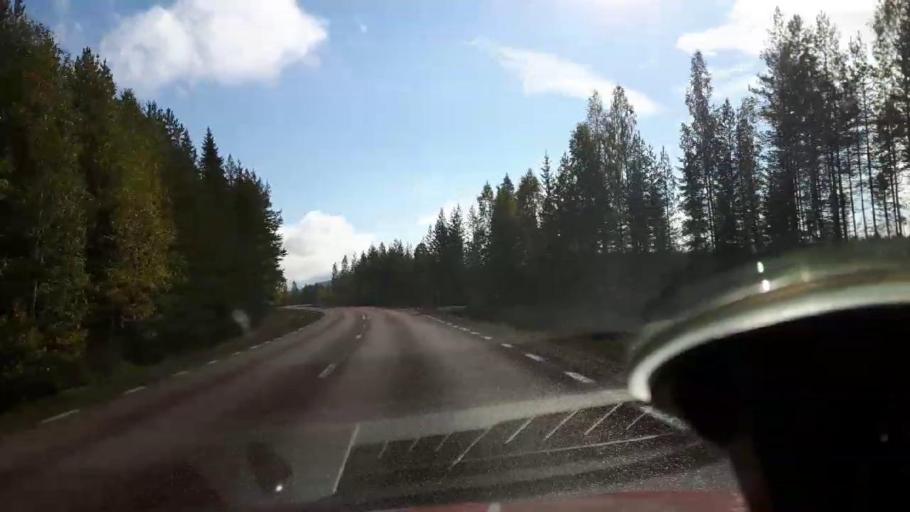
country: SE
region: Gaevleborg
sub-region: Ljusdals Kommun
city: Farila
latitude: 61.9016
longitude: 15.6416
